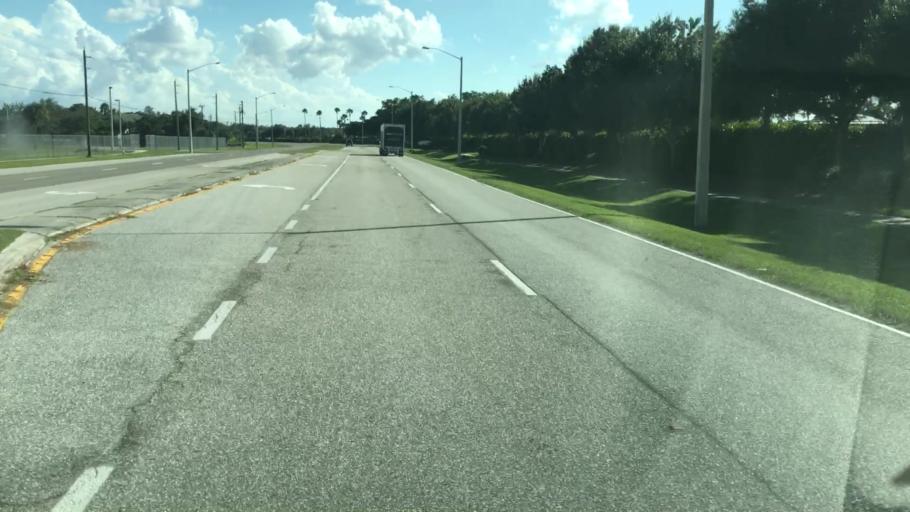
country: US
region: Florida
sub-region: Lee County
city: Fort Myers
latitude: 26.5999
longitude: -81.8179
